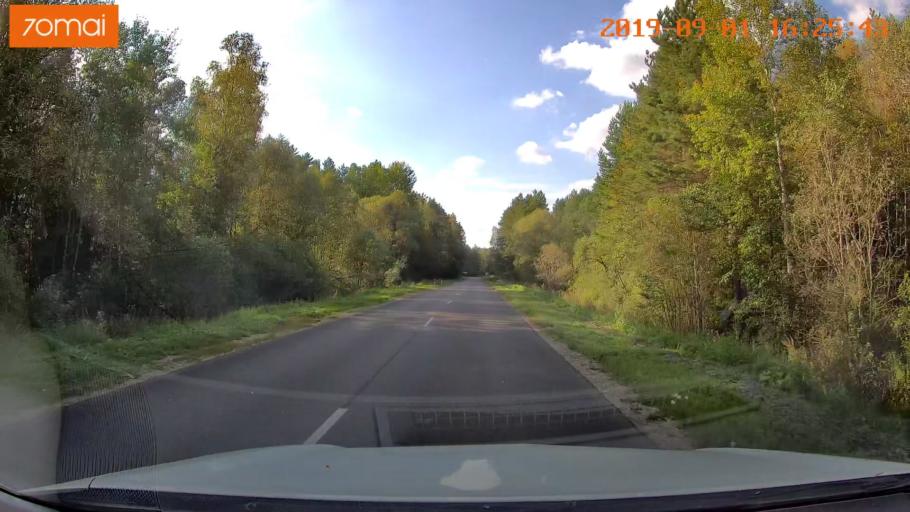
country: RU
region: Kaluga
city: Maloyaroslavets
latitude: 54.9055
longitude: 36.5128
